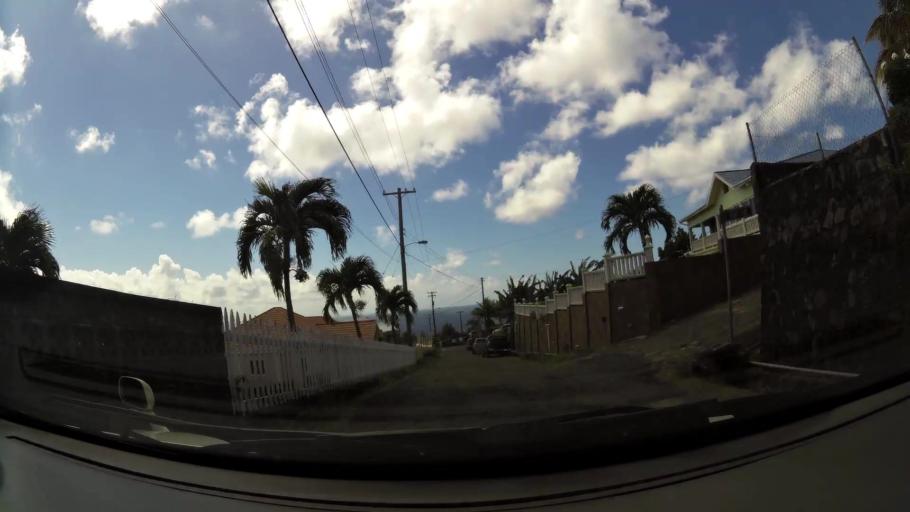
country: VC
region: Saint George
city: Kingstown
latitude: 13.1423
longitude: -61.2233
